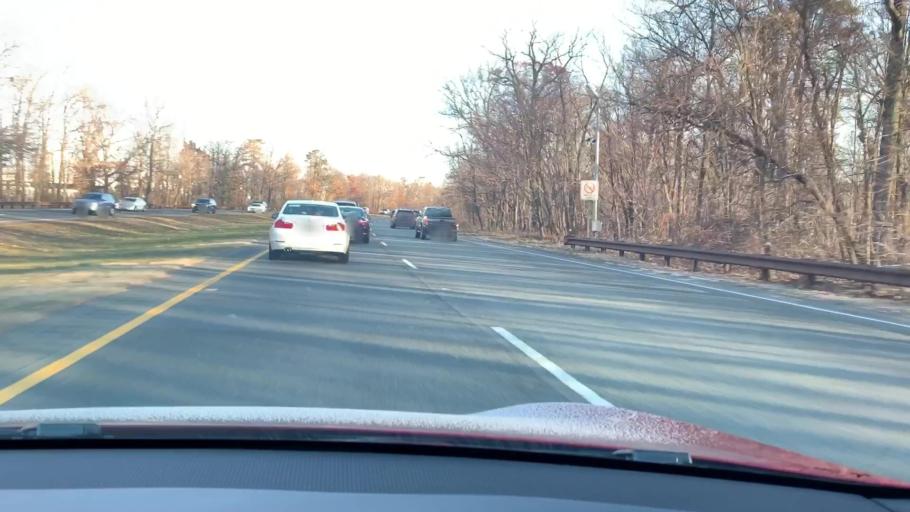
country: US
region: New Jersey
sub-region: Bergen County
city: Englewood Cliffs
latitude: 40.8684
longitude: -73.9540
